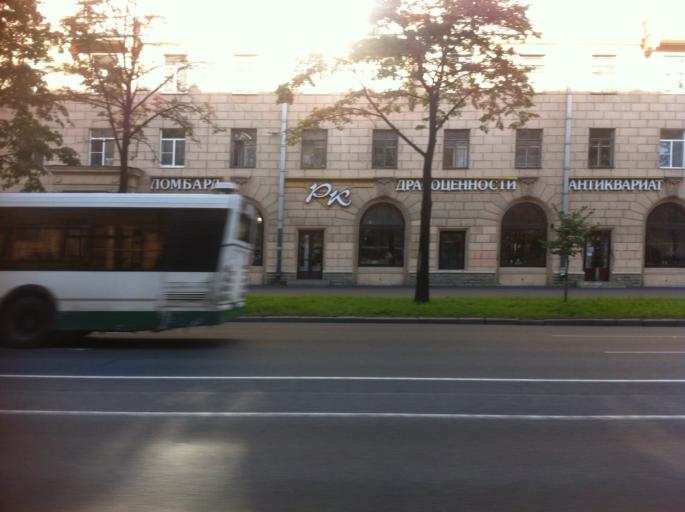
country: RU
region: St.-Petersburg
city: Avtovo
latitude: 59.8716
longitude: 30.2592
